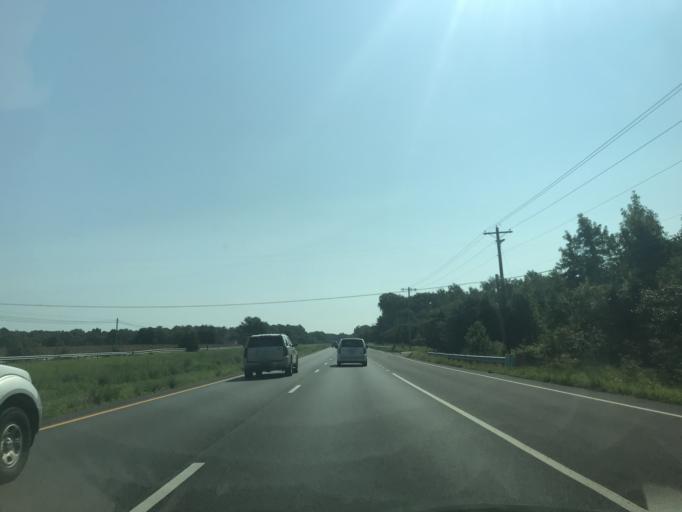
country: US
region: Maryland
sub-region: Charles County
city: Hughesville
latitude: 38.5505
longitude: -76.8201
